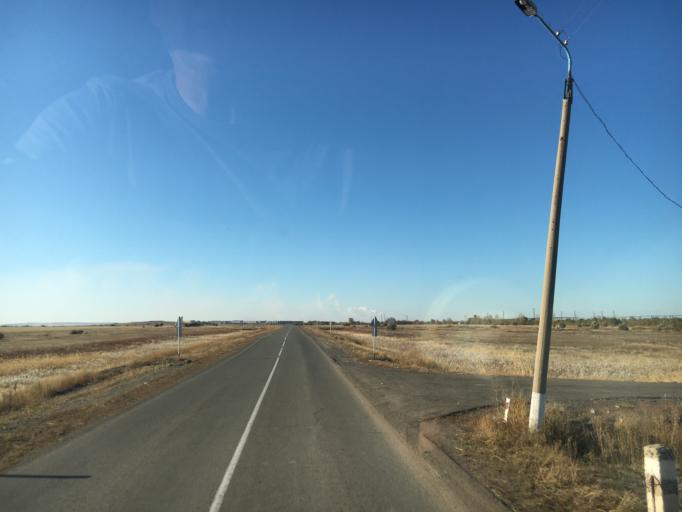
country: KZ
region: Qaraghandy
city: Aqtau
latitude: 50.1926
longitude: 73.0962
